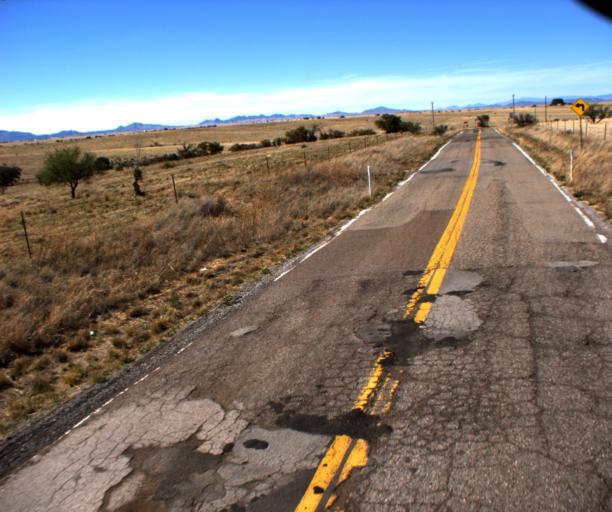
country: US
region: Arizona
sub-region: Cochise County
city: Huachuca City
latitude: 31.5990
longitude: -110.5580
